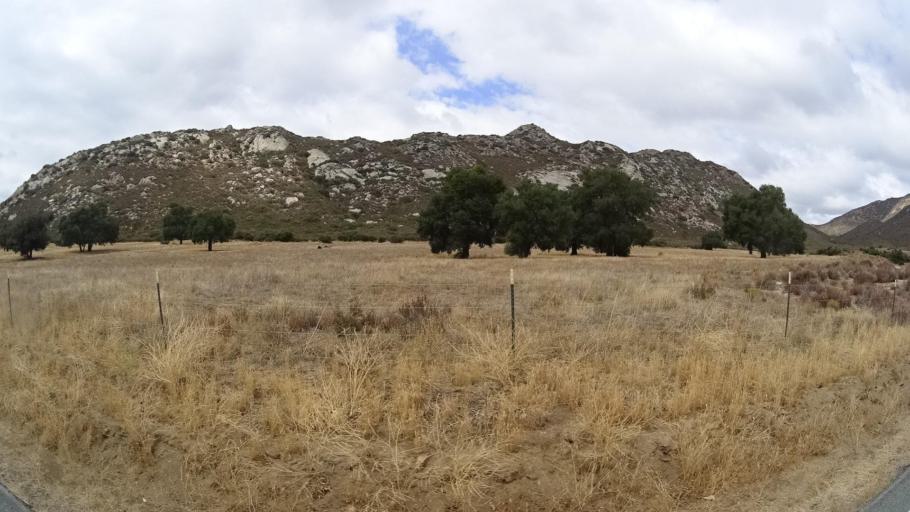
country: US
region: California
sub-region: San Diego County
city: Pine Valley
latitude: 32.7250
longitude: -116.4642
